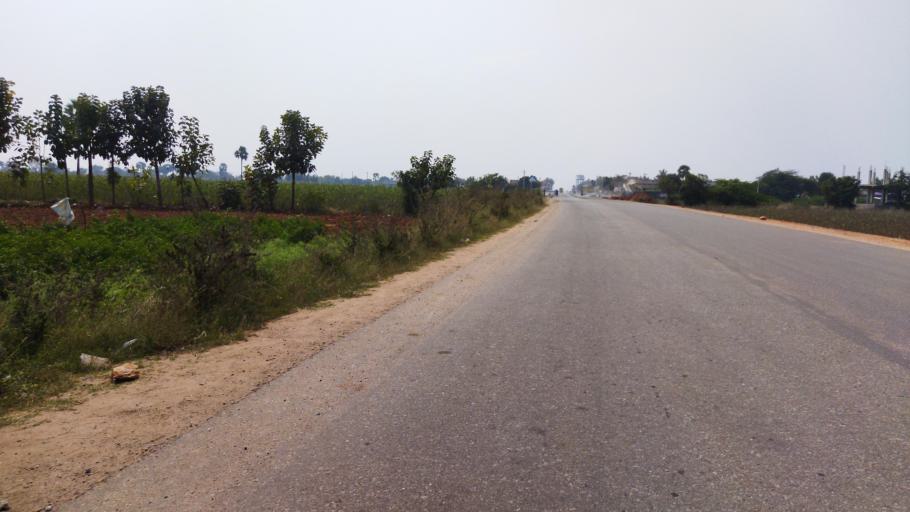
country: IN
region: Telangana
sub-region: Nalgonda
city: Nalgonda
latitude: 17.0949
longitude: 79.3341
